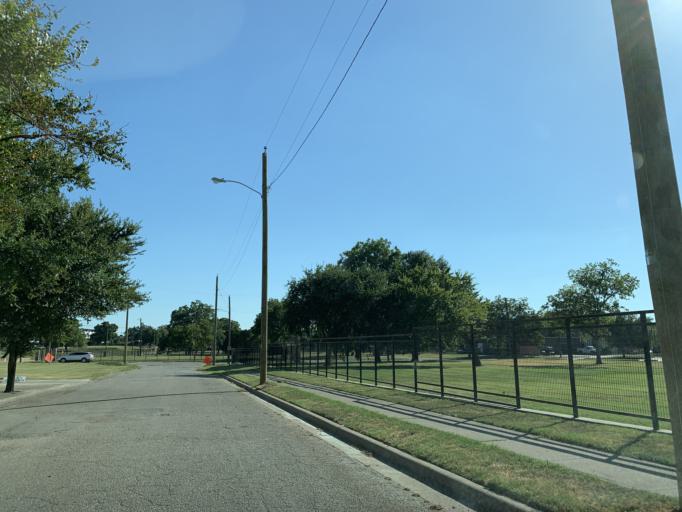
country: US
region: Texas
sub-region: Dallas County
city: Dallas
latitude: 32.7733
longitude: -96.7852
